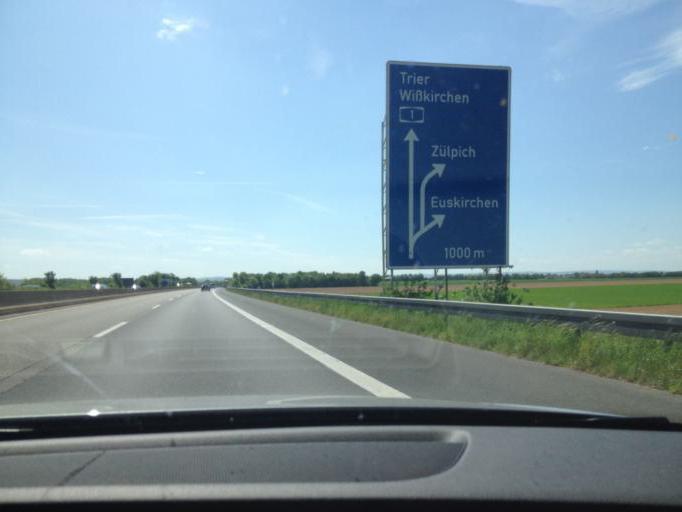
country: DE
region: North Rhine-Westphalia
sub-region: Regierungsbezirk Koln
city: Euskirchen
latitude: 50.6910
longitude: 6.7637
